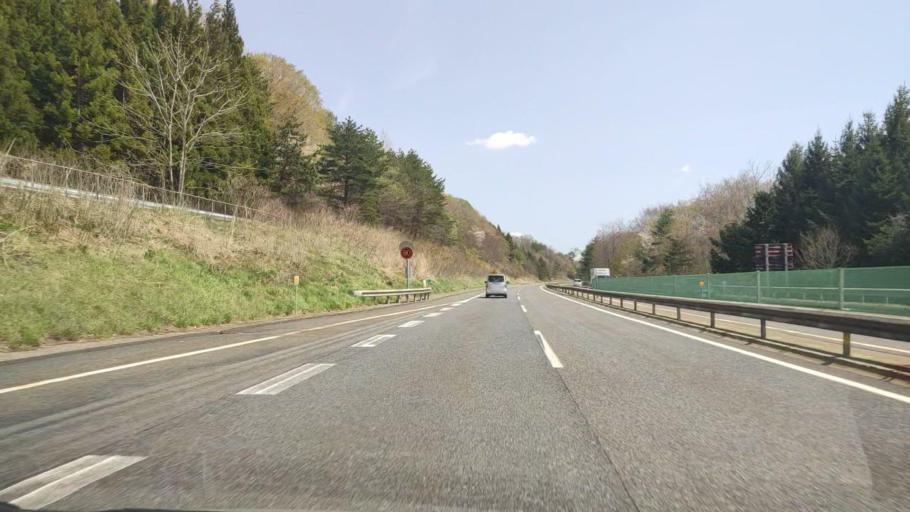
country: JP
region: Iwate
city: Ichinohe
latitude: 40.2125
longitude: 141.2207
